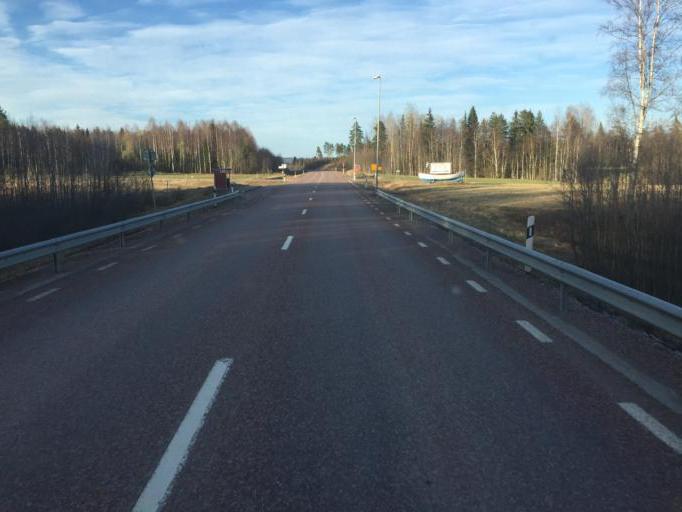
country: SE
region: Dalarna
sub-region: Gagnefs Kommun
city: Gagnef
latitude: 60.5375
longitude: 15.0513
